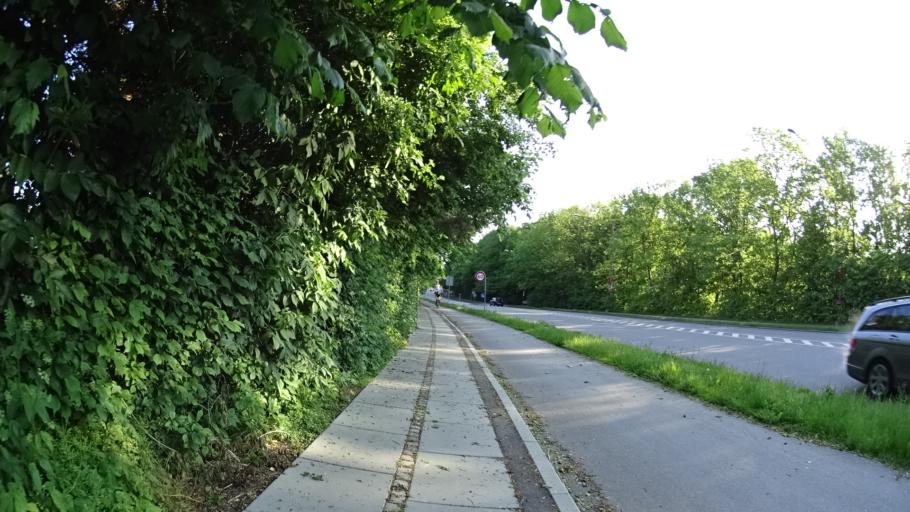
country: DK
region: Central Jutland
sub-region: Arhus Kommune
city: Arhus
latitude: 56.1336
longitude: 10.1899
